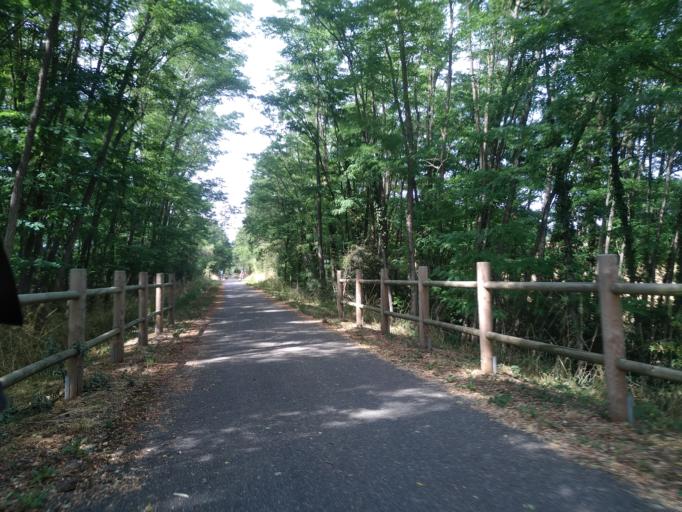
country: FR
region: Bourgogne
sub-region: Departement de Saone-et-Loire
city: Bourbon-Lancy
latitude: 46.5836
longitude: 3.7453
